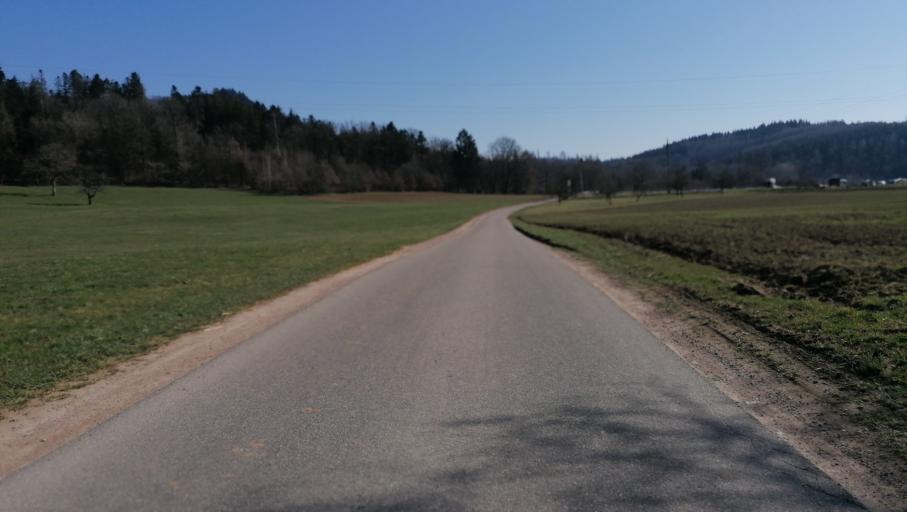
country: CH
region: Aargau
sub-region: Bezirk Rheinfelden
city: Mumpf
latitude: 47.5856
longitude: 7.9179
